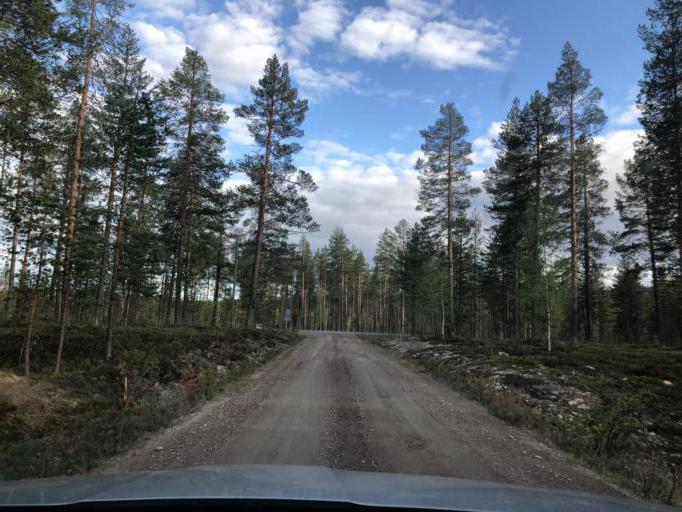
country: SE
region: Norrbotten
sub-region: Arvidsjaurs Kommun
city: Arvidsjaur
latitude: 65.6128
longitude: 19.0617
